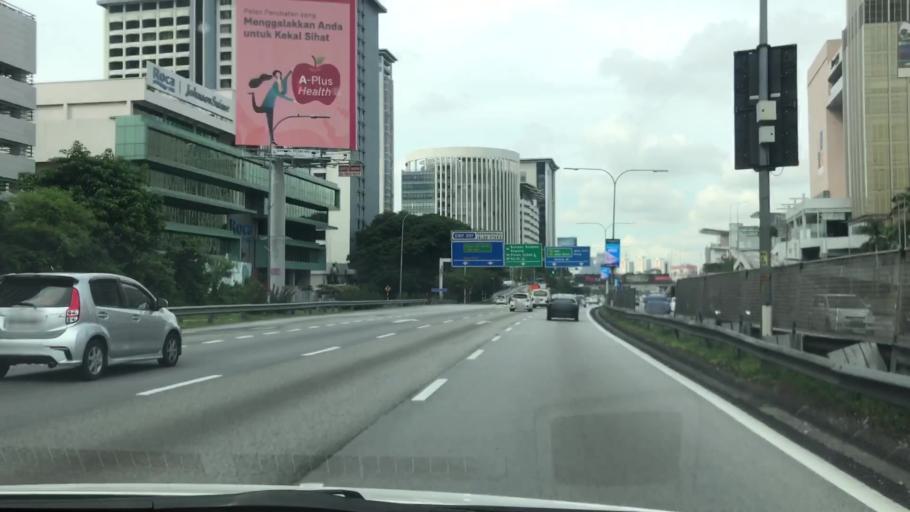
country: MY
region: Selangor
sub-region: Petaling
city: Petaling Jaya
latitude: 3.1042
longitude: 101.6423
